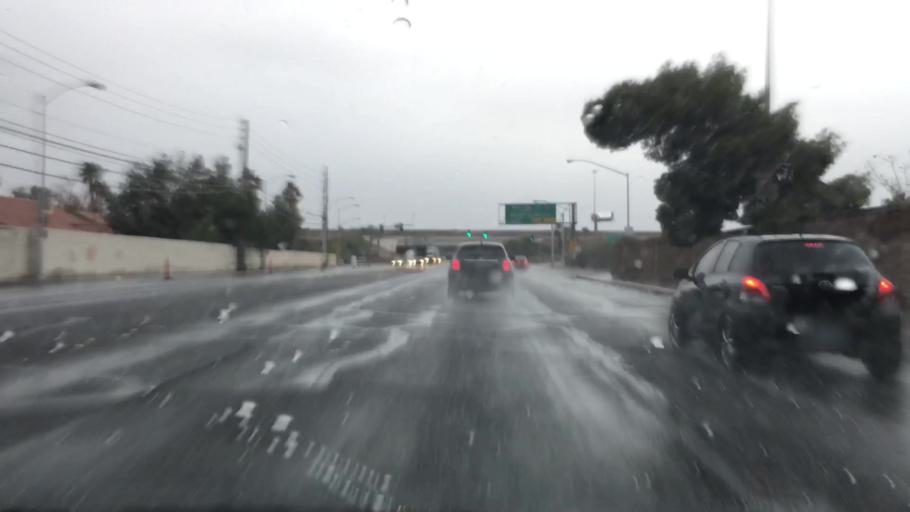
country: US
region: Nevada
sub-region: Clark County
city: Paradise
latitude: 36.0575
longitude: -115.1360
